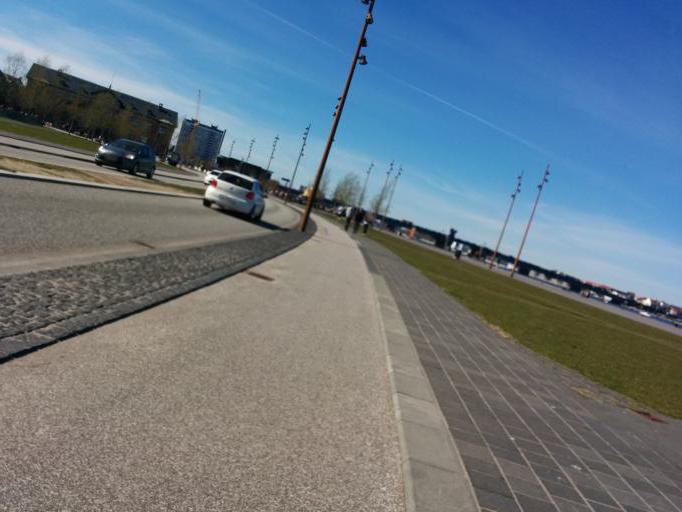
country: DK
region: North Denmark
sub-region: Alborg Kommune
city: Aalborg
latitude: 57.0498
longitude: 9.9253
